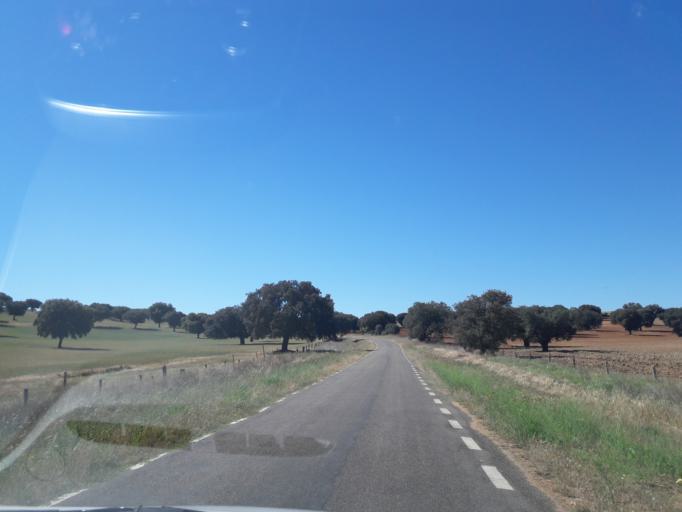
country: ES
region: Castille and Leon
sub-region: Provincia de Salamanca
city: Parada de Arriba
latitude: 41.0069
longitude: -5.8138
